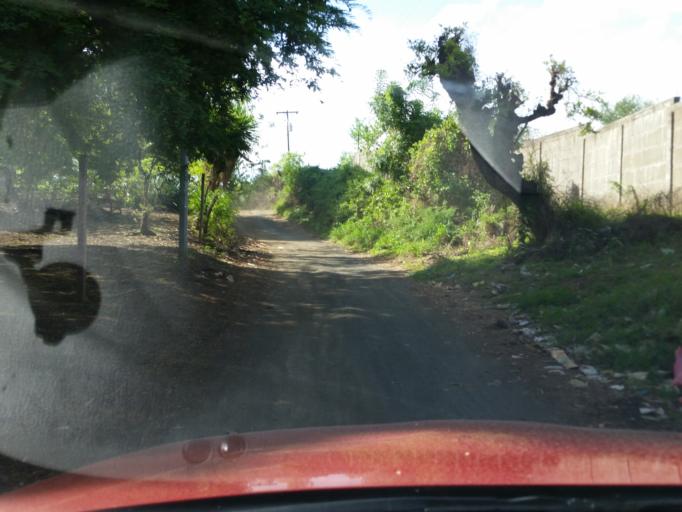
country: NI
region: Managua
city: Managua
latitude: 12.0771
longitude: -86.2555
